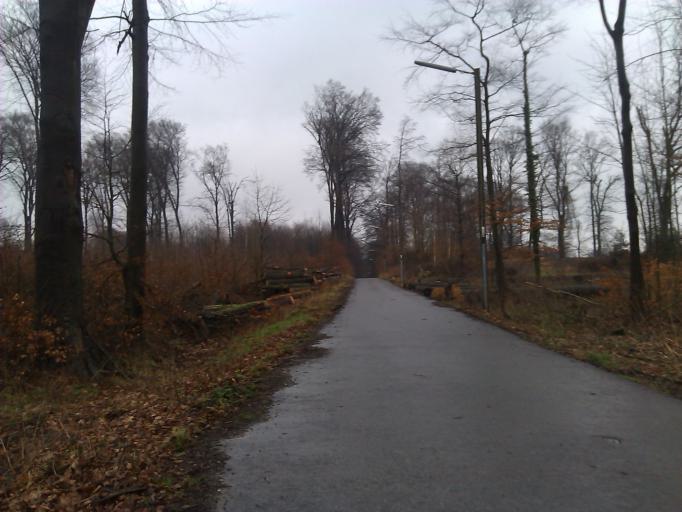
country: DE
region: North Rhine-Westphalia
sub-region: Regierungsbezirk Dusseldorf
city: Ratingen
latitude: 51.3075
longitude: 6.8703
